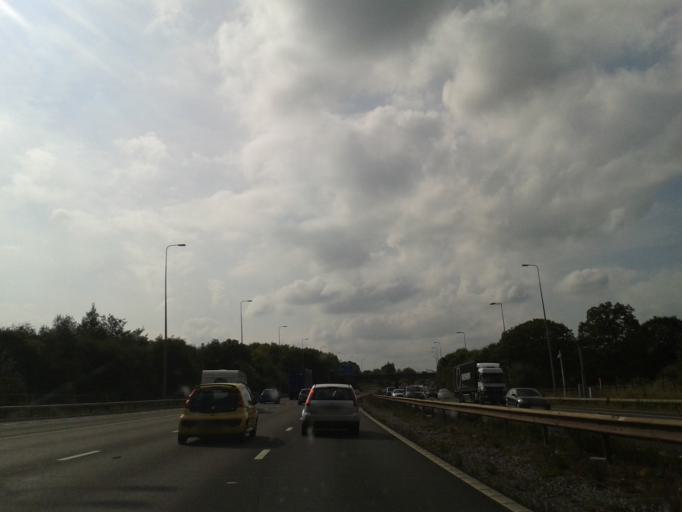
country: GB
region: England
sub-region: Solihull
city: Cheswick Green
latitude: 52.3701
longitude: -1.7932
